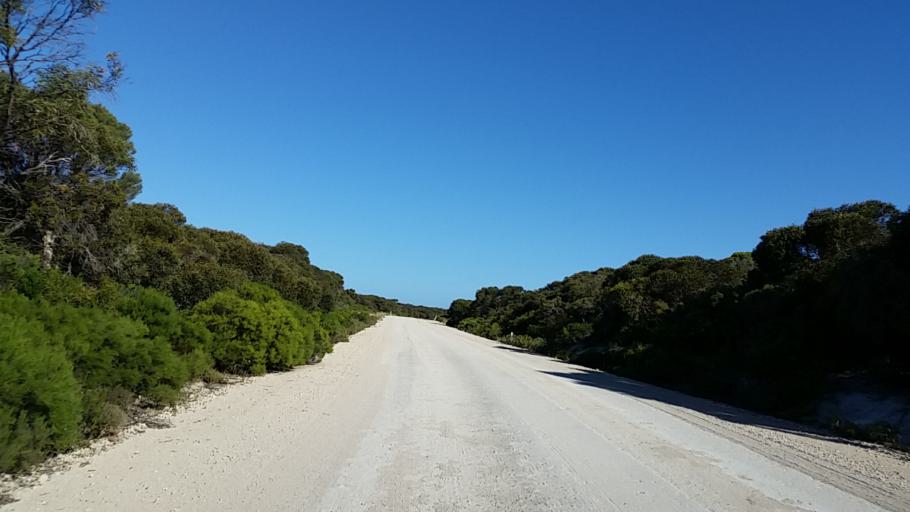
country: AU
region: South Australia
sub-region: Yorke Peninsula
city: Honiton
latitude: -35.2269
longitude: 137.1053
